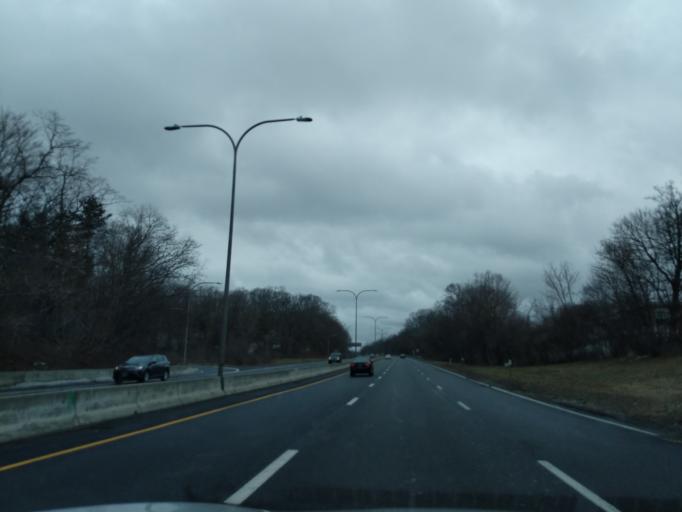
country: US
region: Rhode Island
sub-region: Providence County
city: North Providence
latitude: 41.9027
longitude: -71.4472
